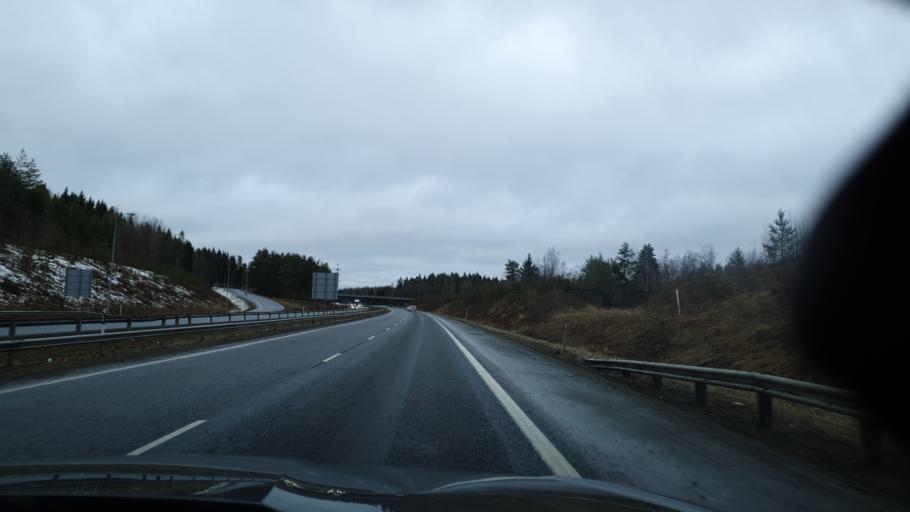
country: FI
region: Pirkanmaa
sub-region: Tampere
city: Lempaeaelae
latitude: 61.3925
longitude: 23.7866
